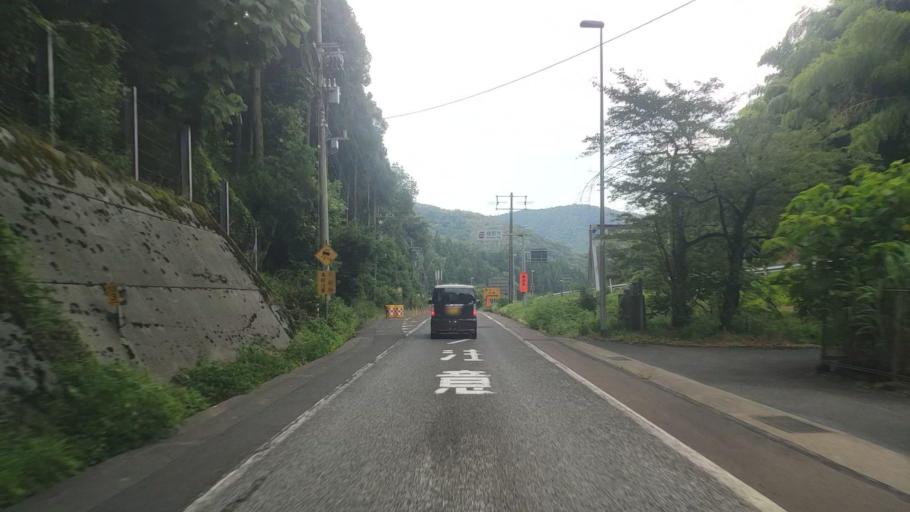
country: JP
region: Fukui
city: Takefu
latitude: 35.8479
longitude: 136.1254
